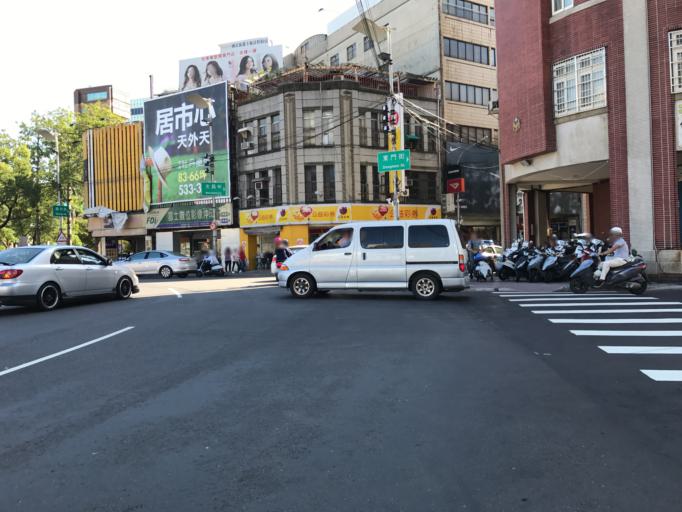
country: TW
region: Taiwan
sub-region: Hsinchu
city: Hsinchu
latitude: 24.8043
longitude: 120.9700
